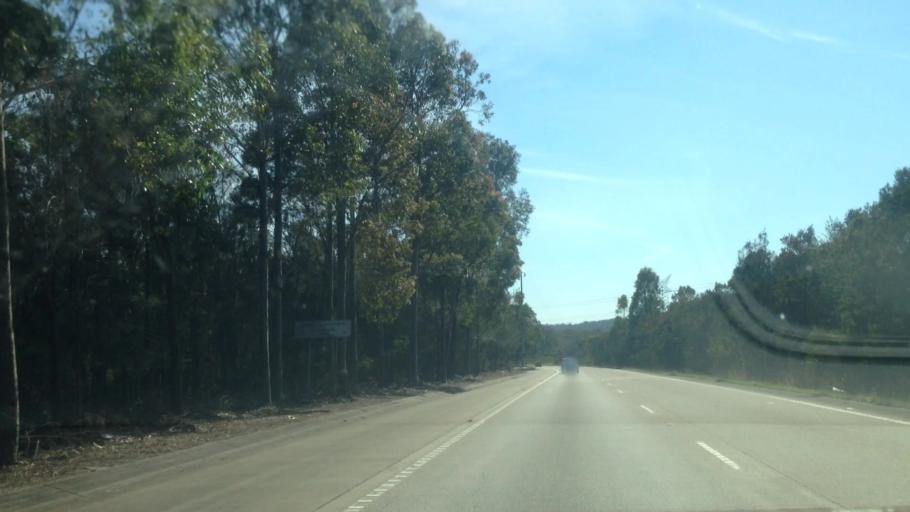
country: AU
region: New South Wales
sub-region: Lake Macquarie Shire
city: Fennell Bay
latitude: -32.9580
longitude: 151.5421
